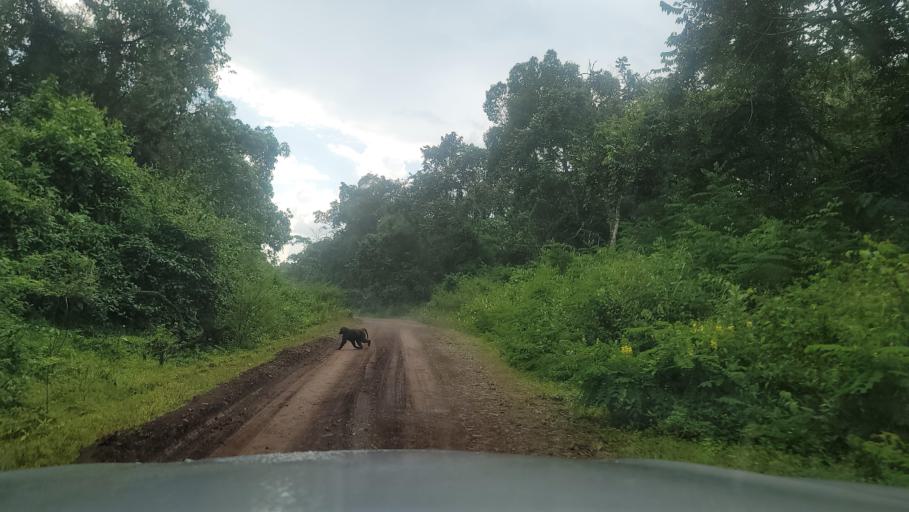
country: ET
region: Southern Nations, Nationalities, and People's Region
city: Bonga
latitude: 7.6427
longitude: 36.2389
